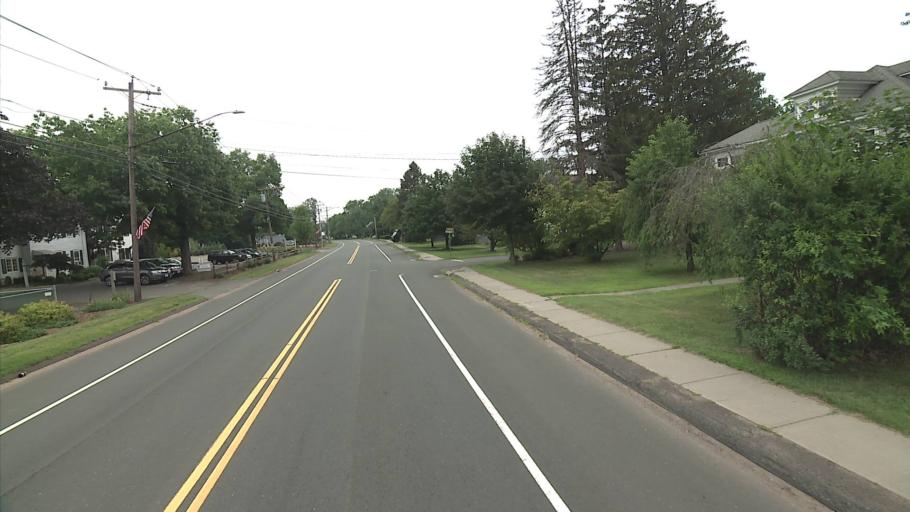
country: US
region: Connecticut
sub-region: Middlesex County
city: Cromwell
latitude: 41.6249
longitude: -72.6530
